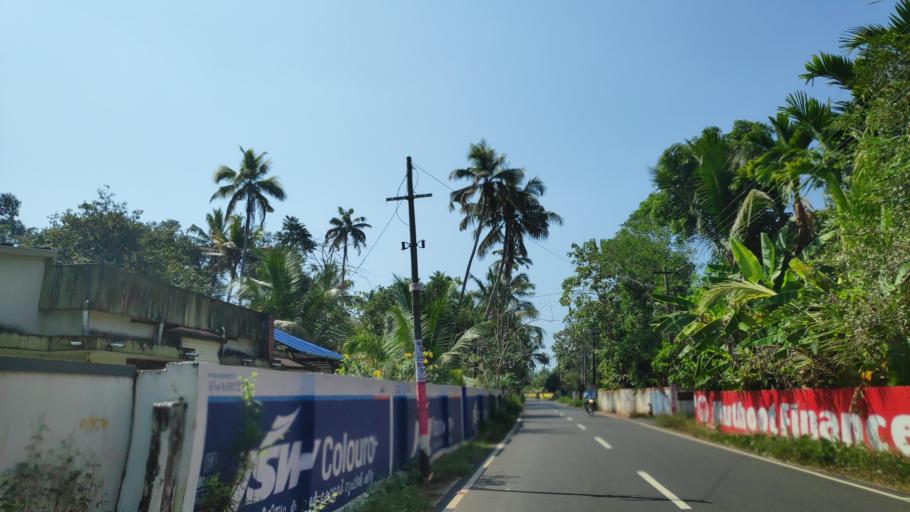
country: IN
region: Kerala
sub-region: Alappuzha
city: Shertallai
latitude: 9.6567
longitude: 76.3291
